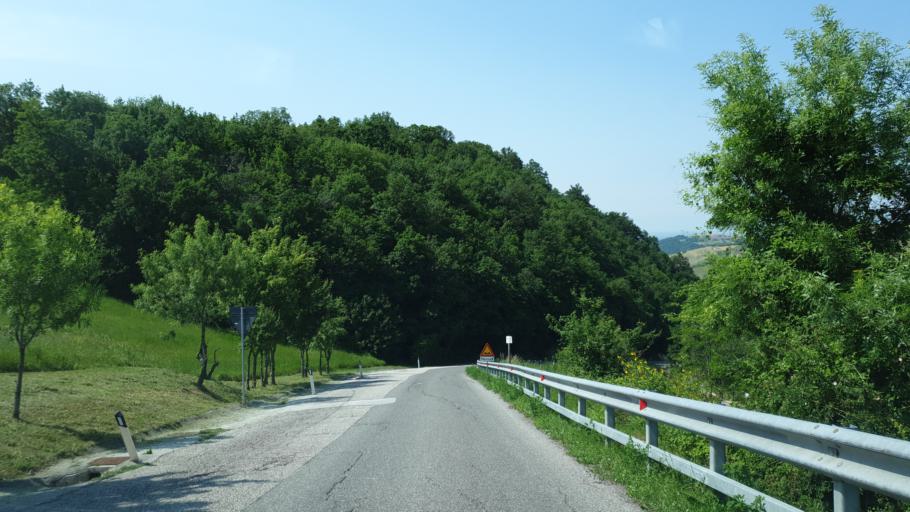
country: SM
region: San Marino
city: San Marino
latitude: 43.9382
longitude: 12.4332
